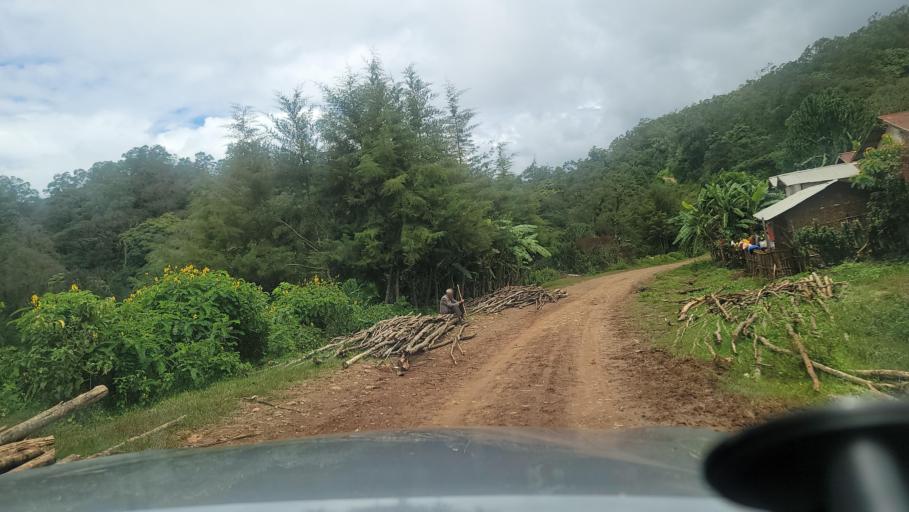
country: ET
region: Southern Nations, Nationalities, and People's Region
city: Bonga
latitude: 7.6310
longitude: 36.2213
